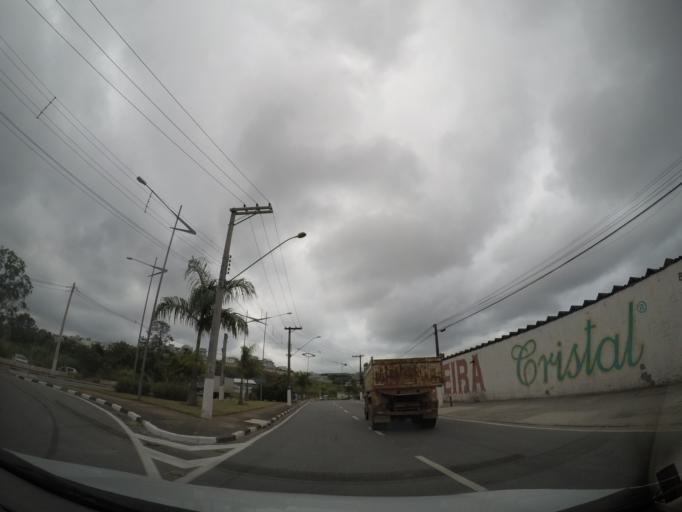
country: BR
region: Sao Paulo
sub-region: Aruja
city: Aruja
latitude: -23.4141
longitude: -46.3240
